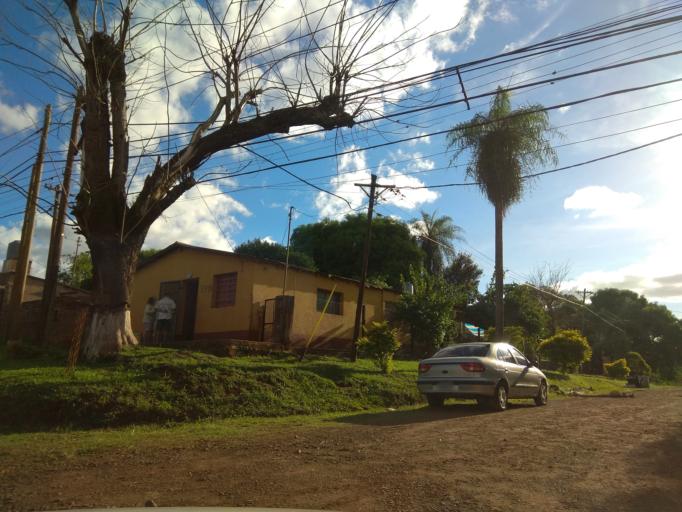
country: AR
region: Misiones
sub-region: Departamento de Capital
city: Posadas
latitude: -27.3956
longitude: -55.9281
